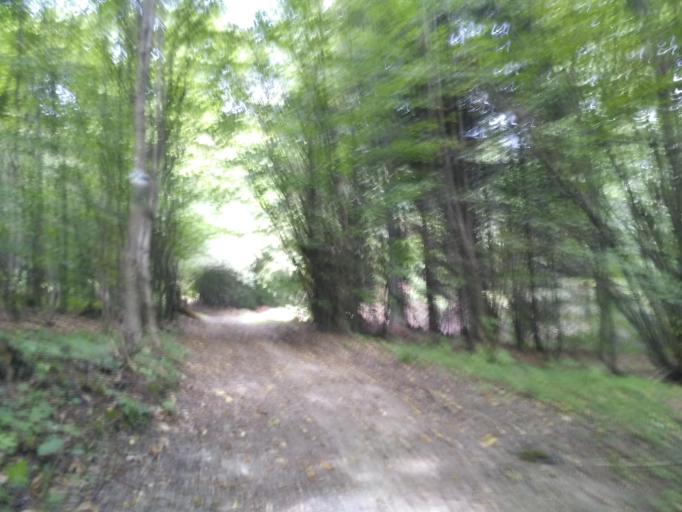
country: PL
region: Subcarpathian Voivodeship
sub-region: Powiat strzyzowski
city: Frysztak
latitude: 49.8863
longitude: 21.5470
